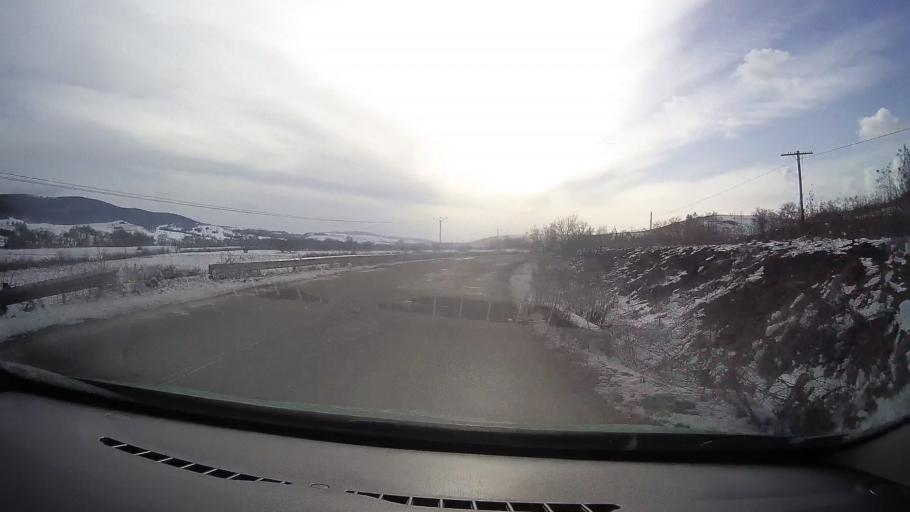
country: RO
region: Sibiu
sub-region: Comuna Iacobeni
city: Iacobeni
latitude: 46.0319
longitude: 24.7168
